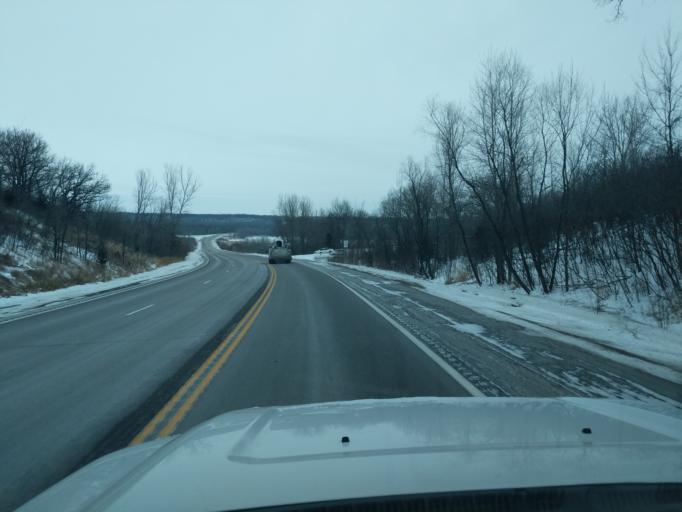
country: US
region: Minnesota
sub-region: Redwood County
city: Redwood Falls
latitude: 44.5595
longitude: -94.9993
